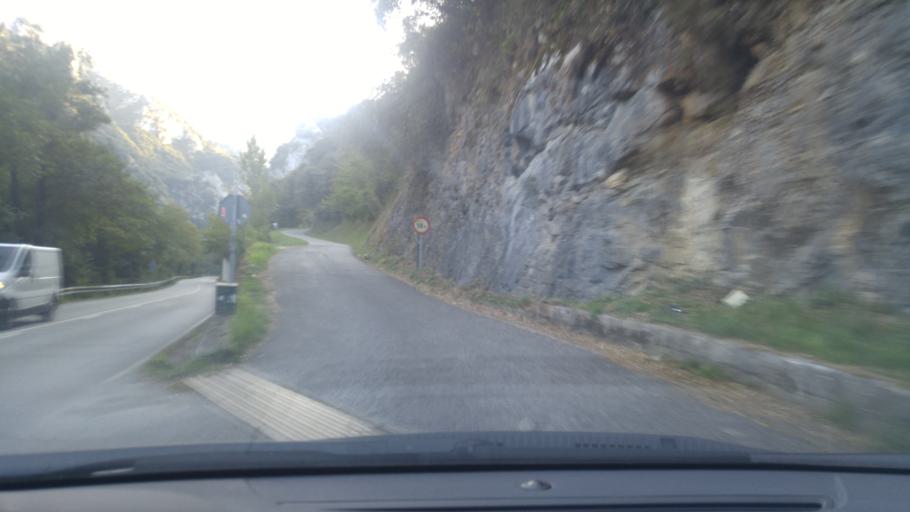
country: ES
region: Asturias
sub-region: Province of Asturias
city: Proaza
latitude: 43.2496
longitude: -6.0241
